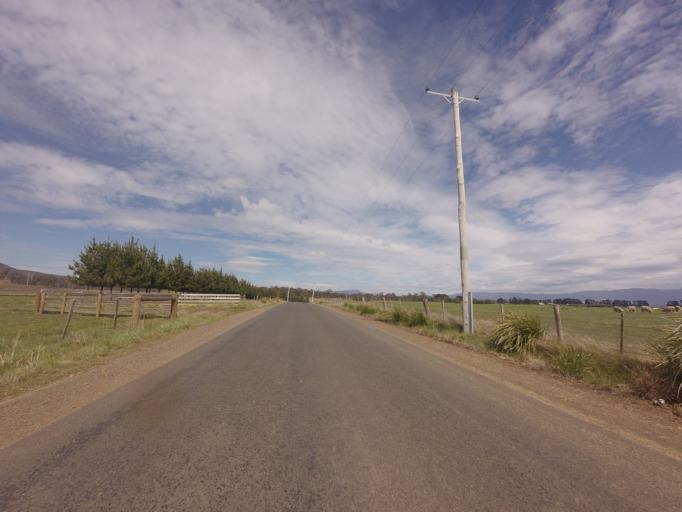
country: AU
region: Tasmania
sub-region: Northern Midlands
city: Longford
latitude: -41.7056
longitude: 147.1967
